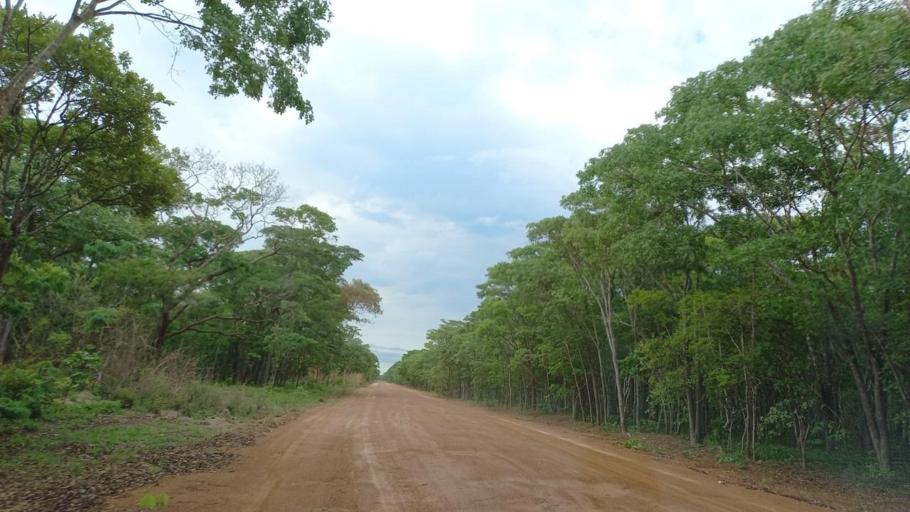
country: ZM
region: North-Western
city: Kalengwa
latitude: -13.3701
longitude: 25.0741
